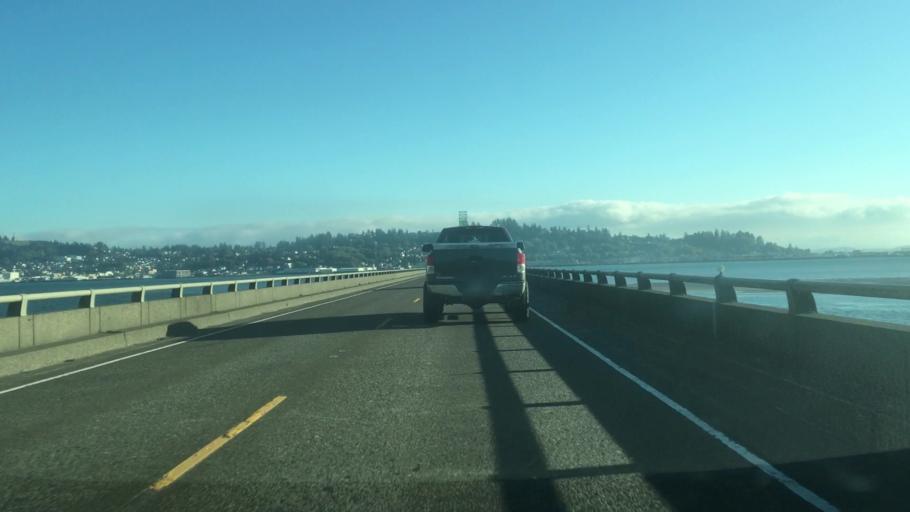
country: US
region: Oregon
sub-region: Clatsop County
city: Astoria
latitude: 46.2092
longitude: -123.8588
